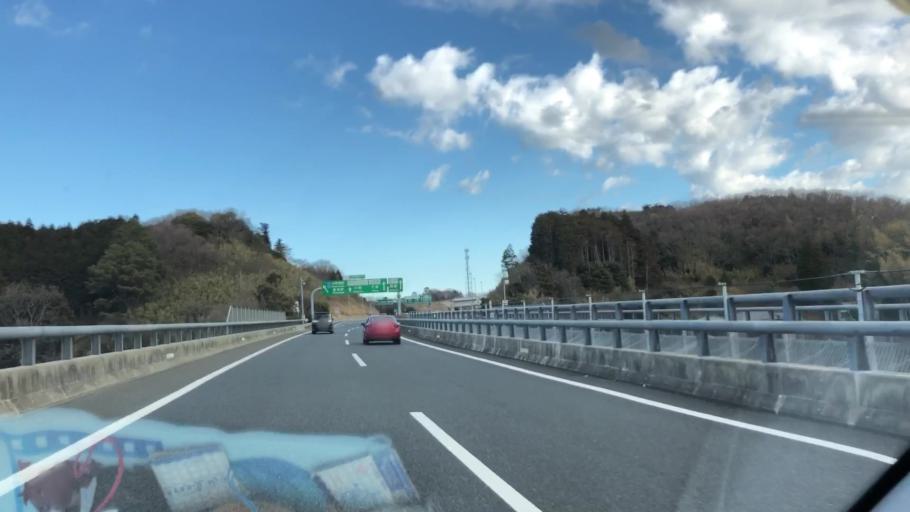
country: JP
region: Chiba
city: Kisarazu
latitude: 35.3501
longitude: 139.9454
